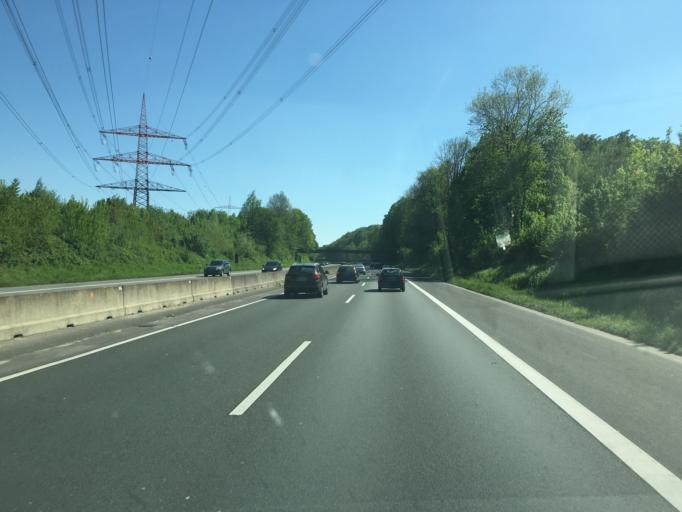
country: DE
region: North Rhine-Westphalia
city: Castrop-Rauxel
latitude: 51.5538
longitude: 7.3572
